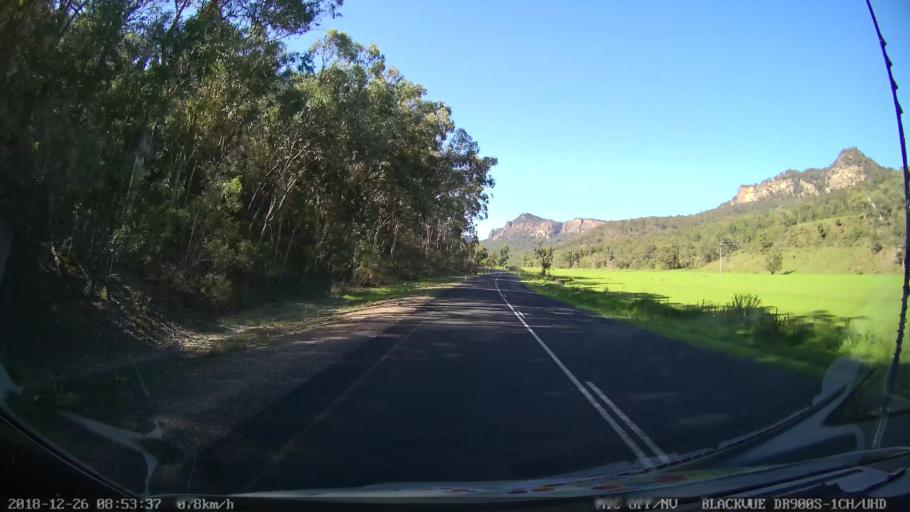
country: AU
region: New South Wales
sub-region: Mid-Western Regional
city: Kandos
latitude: -32.6061
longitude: 150.0767
